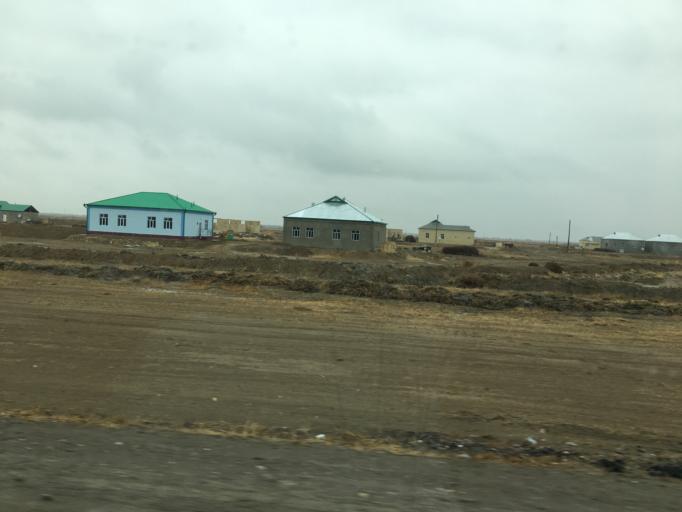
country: TM
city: Murgab
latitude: 37.4733
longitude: 62.0221
